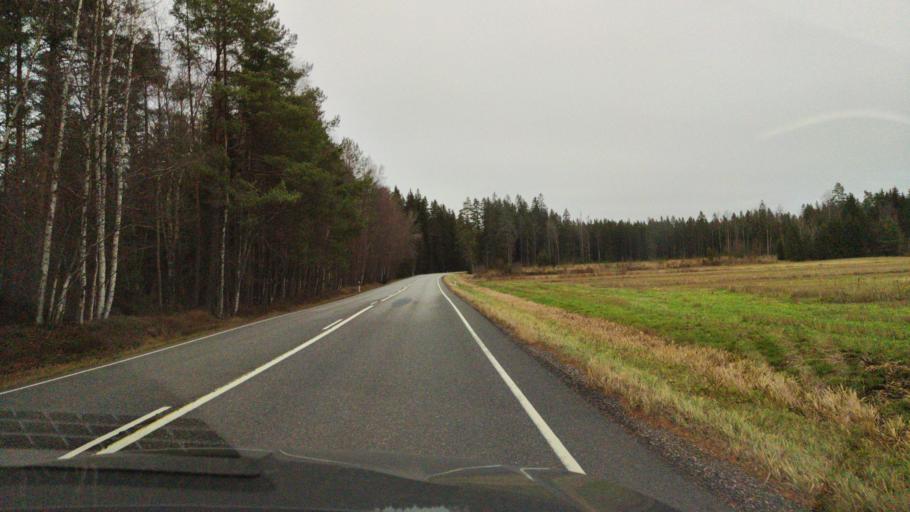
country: FI
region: Varsinais-Suomi
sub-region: Loimaa
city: Ylaene
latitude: 60.7517
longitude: 22.4272
